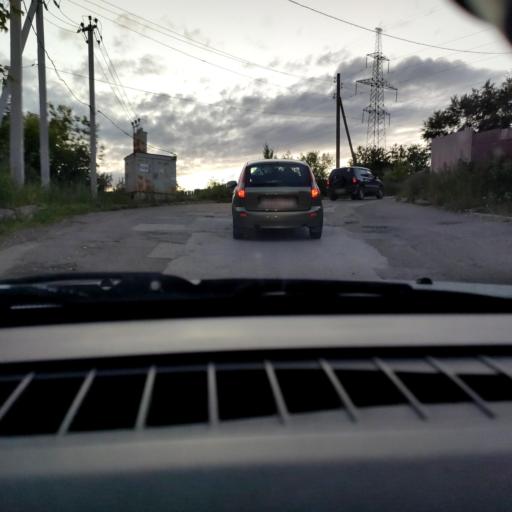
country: RU
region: Perm
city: Perm
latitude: 58.1173
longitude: 56.3094
